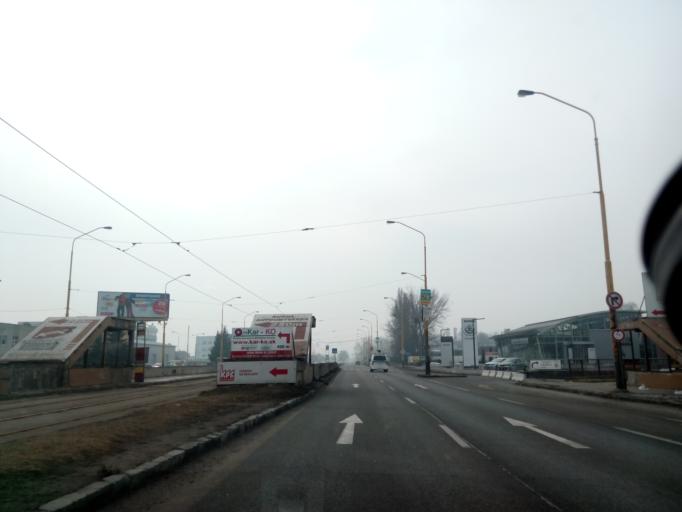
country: SK
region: Kosicky
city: Kosice
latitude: 48.6833
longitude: 21.2675
